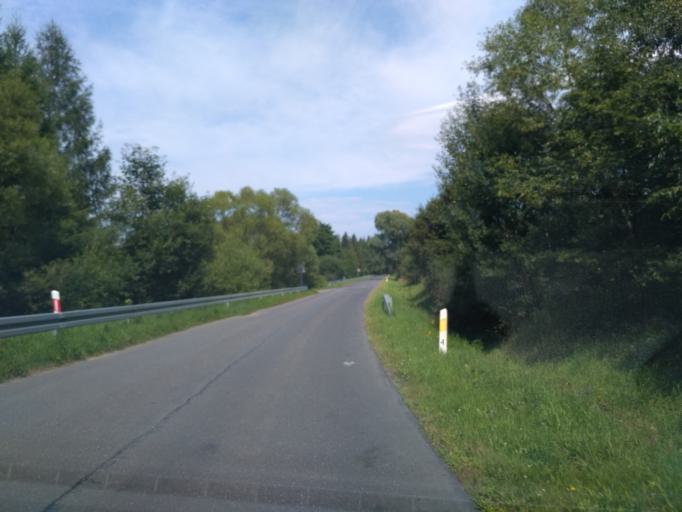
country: PL
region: Subcarpathian Voivodeship
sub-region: Powiat leski
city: Polanczyk
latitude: 49.3082
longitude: 22.5227
